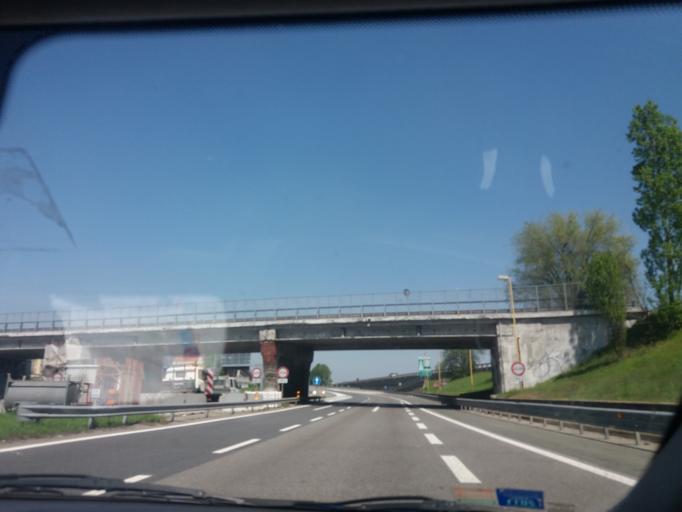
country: IT
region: Piedmont
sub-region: Provincia di Torino
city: Fornaci
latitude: 45.0240
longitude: 7.6033
